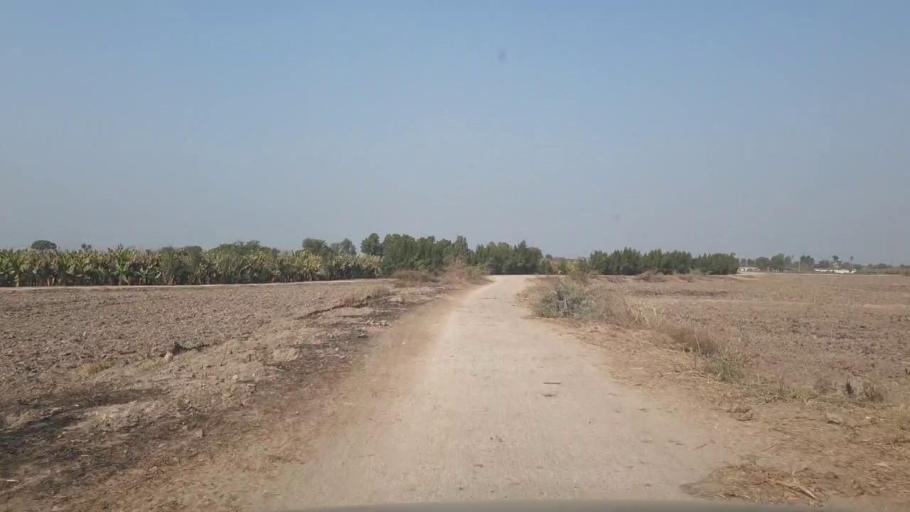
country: PK
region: Sindh
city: Tando Allahyar
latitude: 25.4453
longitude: 68.7869
